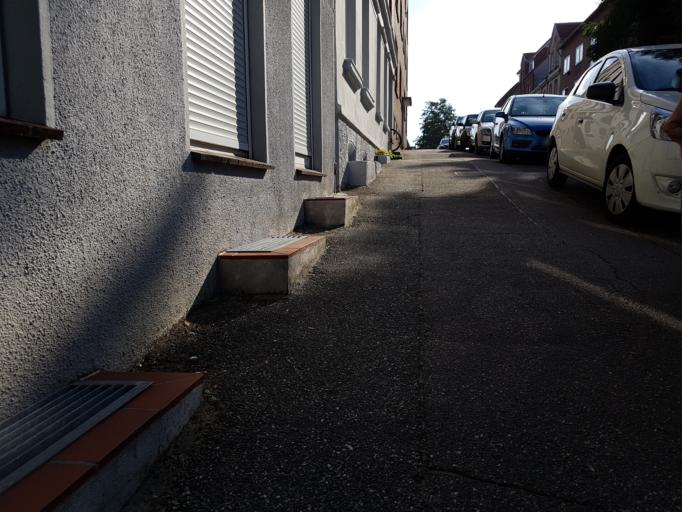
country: DE
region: Schleswig-Holstein
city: Kiel
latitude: 54.3159
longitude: 10.1442
